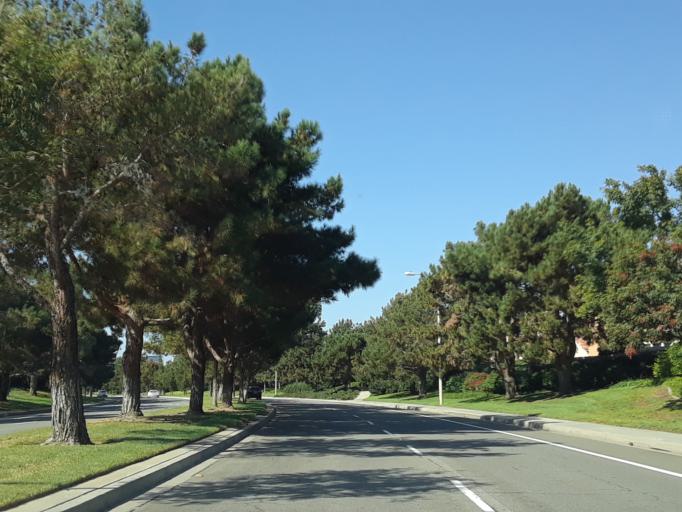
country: US
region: California
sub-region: Orange County
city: Irvine
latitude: 33.6788
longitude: -117.8217
